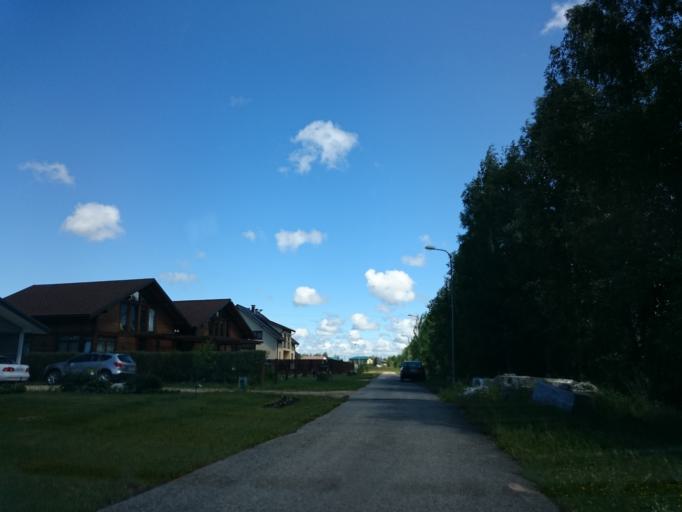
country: LV
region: Adazi
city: Adazi
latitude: 57.0797
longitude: 24.3042
